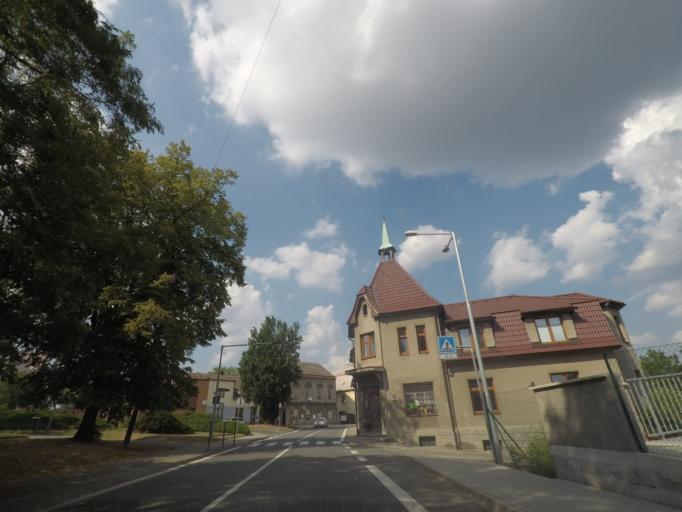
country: CZ
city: Borohradek
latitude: 50.0962
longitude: 16.0917
